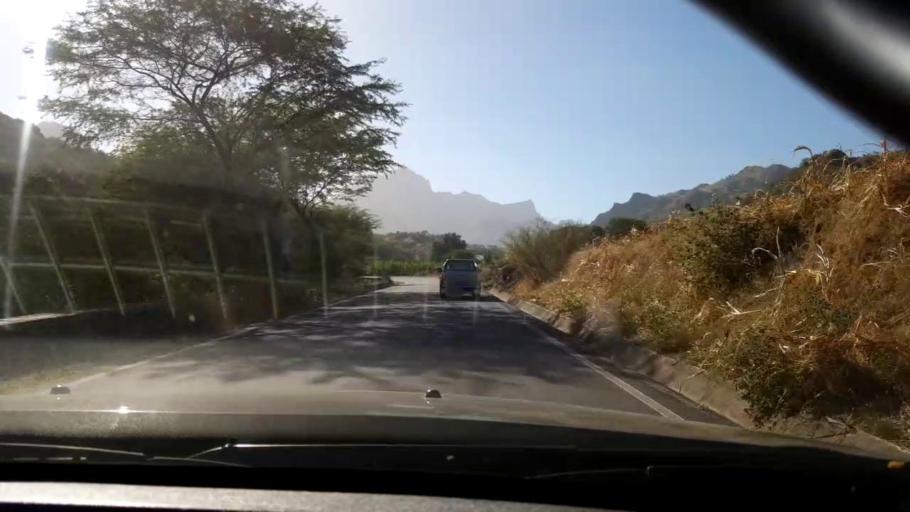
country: CV
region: Sao Lourenco dos Orgaos
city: Joao Teves
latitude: 15.0696
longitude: -23.5729
